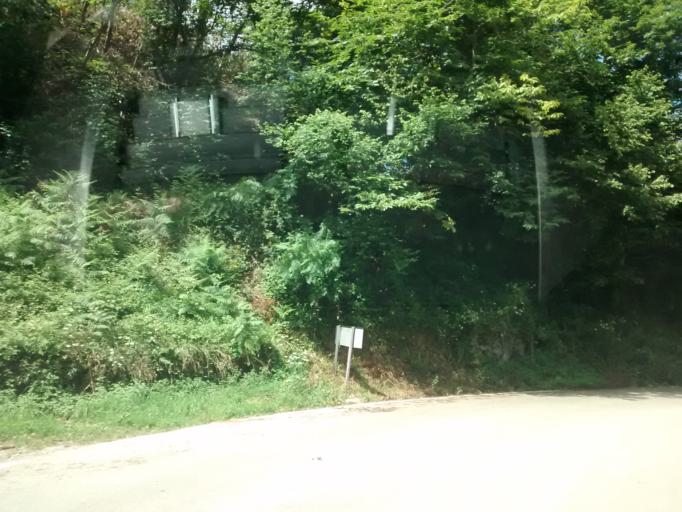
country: ES
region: Cantabria
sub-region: Provincia de Cantabria
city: Ruente
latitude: 43.1884
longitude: -4.2652
